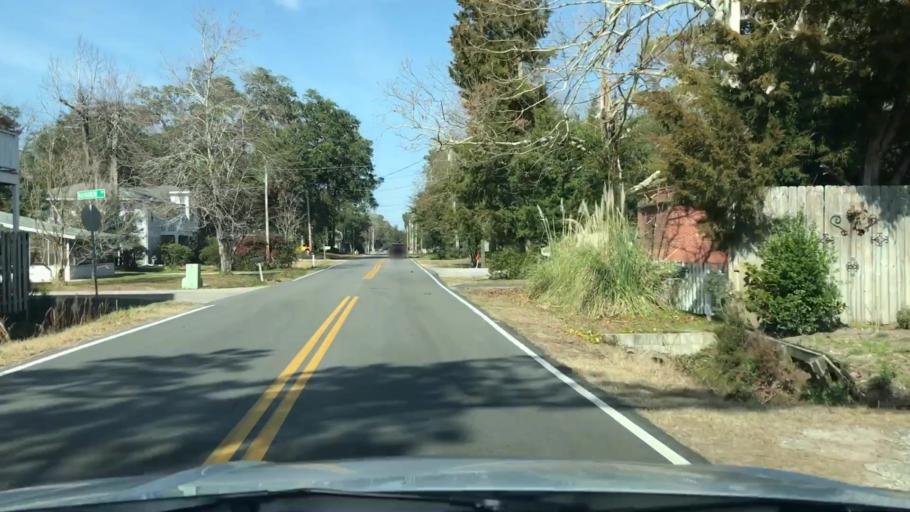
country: US
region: South Carolina
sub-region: Horry County
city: Garden City
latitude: 33.5881
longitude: -78.9942
